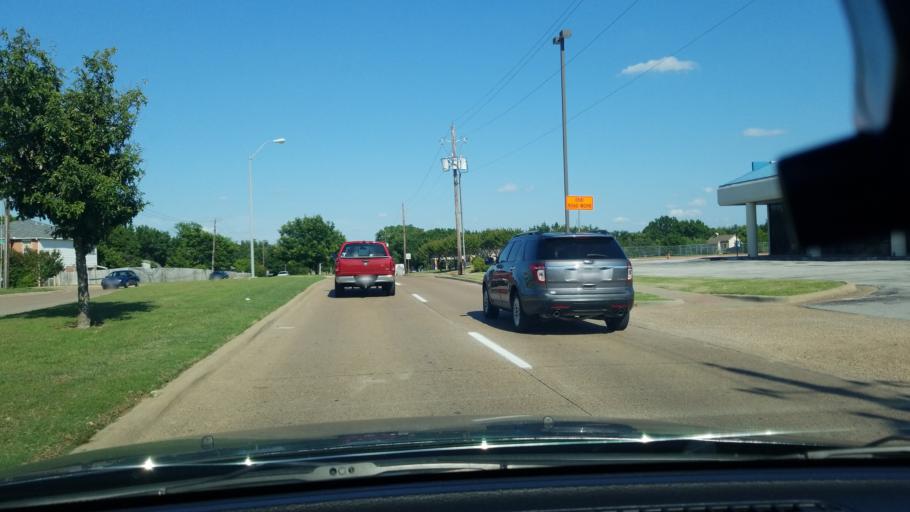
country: US
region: Texas
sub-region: Dallas County
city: Mesquite
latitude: 32.7639
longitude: -96.5815
